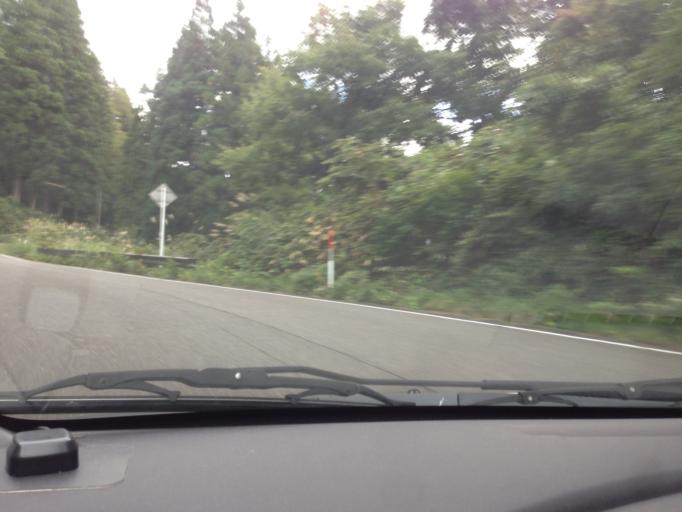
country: JP
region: Fukushima
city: Kitakata
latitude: 37.4571
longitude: 139.7182
